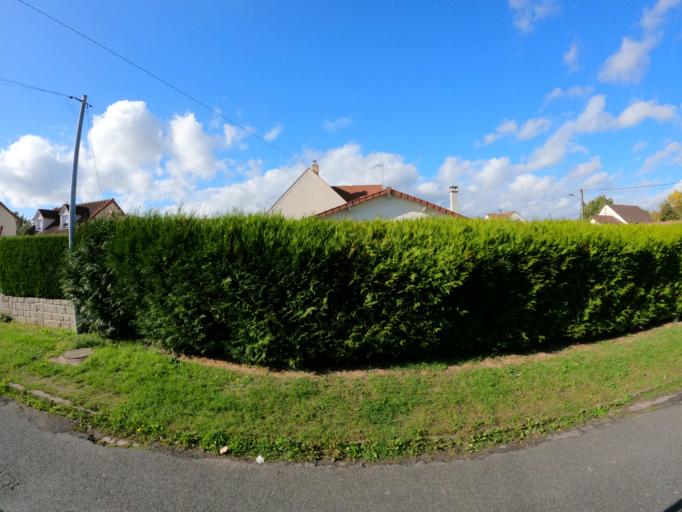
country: FR
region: Ile-de-France
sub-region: Departement de Seine-et-Marne
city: Montry
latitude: 48.8871
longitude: 2.8350
